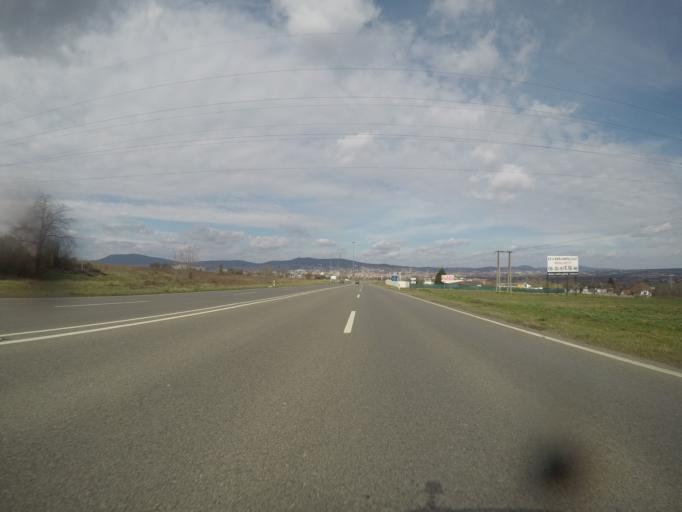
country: HU
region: Baranya
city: Pecs
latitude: 46.0341
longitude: 18.2331
